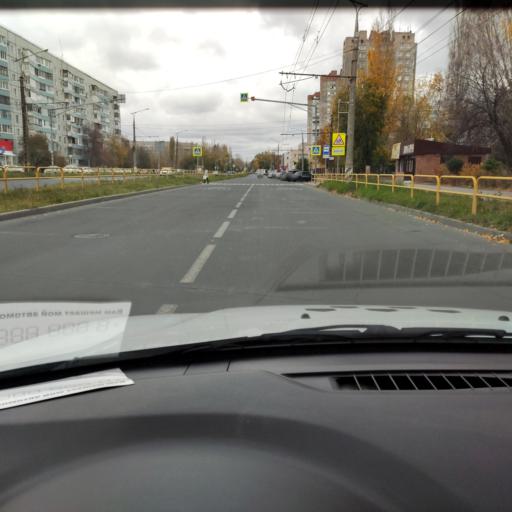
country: RU
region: Samara
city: Tol'yatti
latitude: 53.5057
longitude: 49.4322
